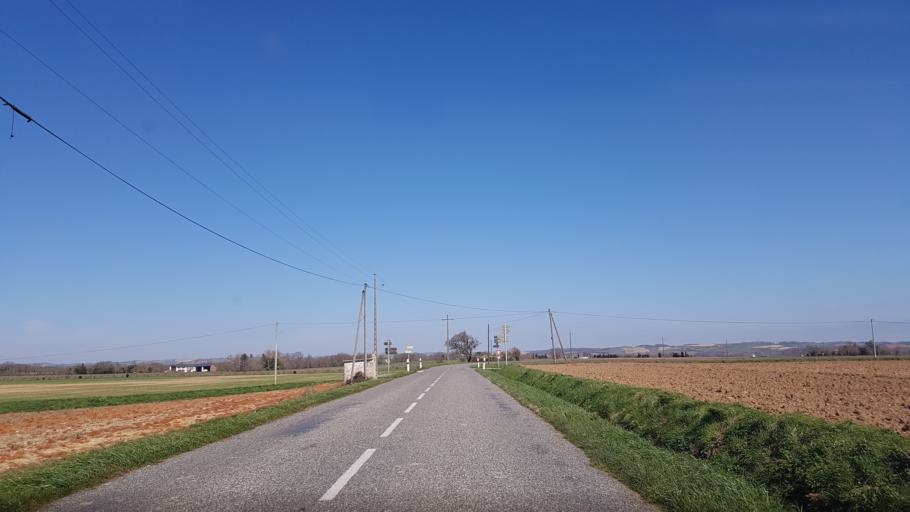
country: FR
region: Languedoc-Roussillon
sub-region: Departement de l'Aude
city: Belpech
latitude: 43.1800
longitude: 1.7118
